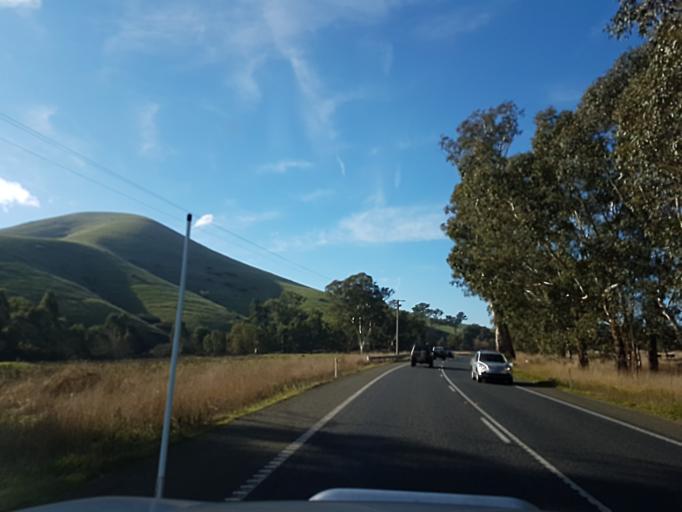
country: AU
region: Victoria
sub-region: Murrindindi
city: Alexandra
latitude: -37.1553
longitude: 145.5670
